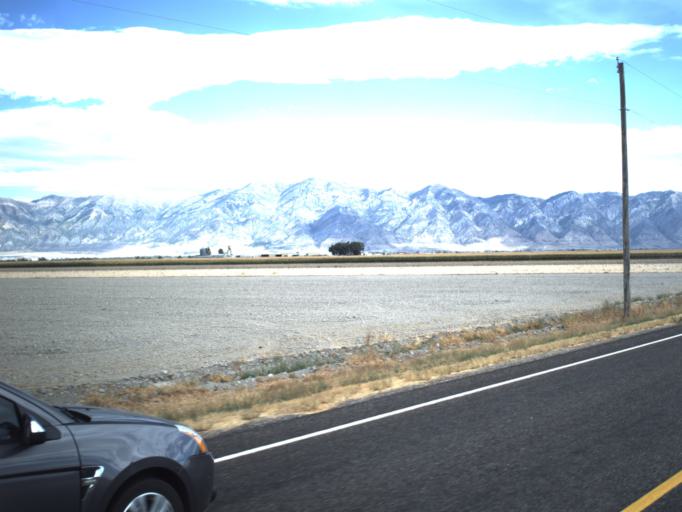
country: US
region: Utah
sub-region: Box Elder County
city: Elwood
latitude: 41.5721
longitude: -112.2117
